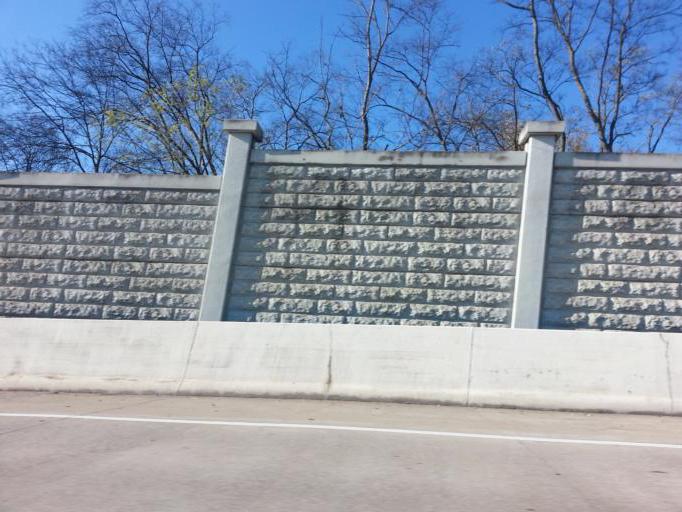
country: US
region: Tennessee
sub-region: Knox County
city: Knoxville
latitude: 35.9784
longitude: -83.9365
